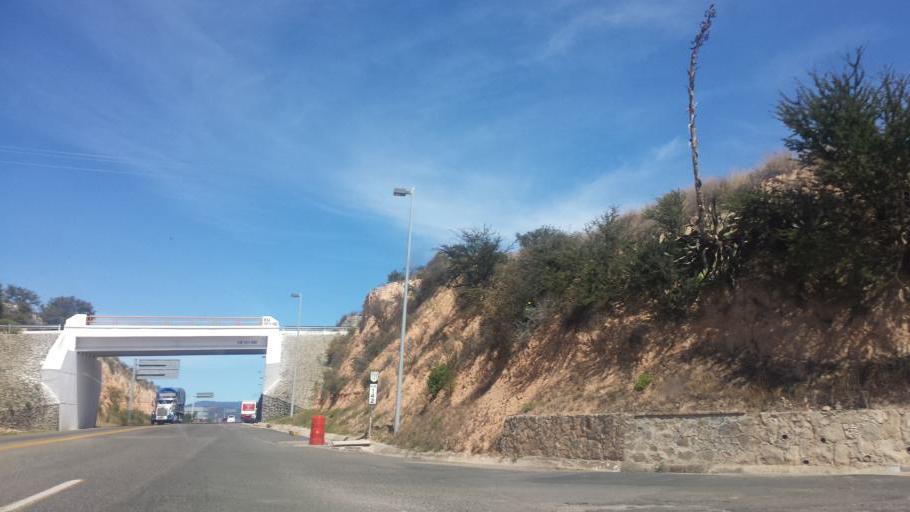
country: MX
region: Oaxaca
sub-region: Villa Tejupam de la Union
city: Villa Tejupam de la Union
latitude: 17.7262
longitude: -97.3528
